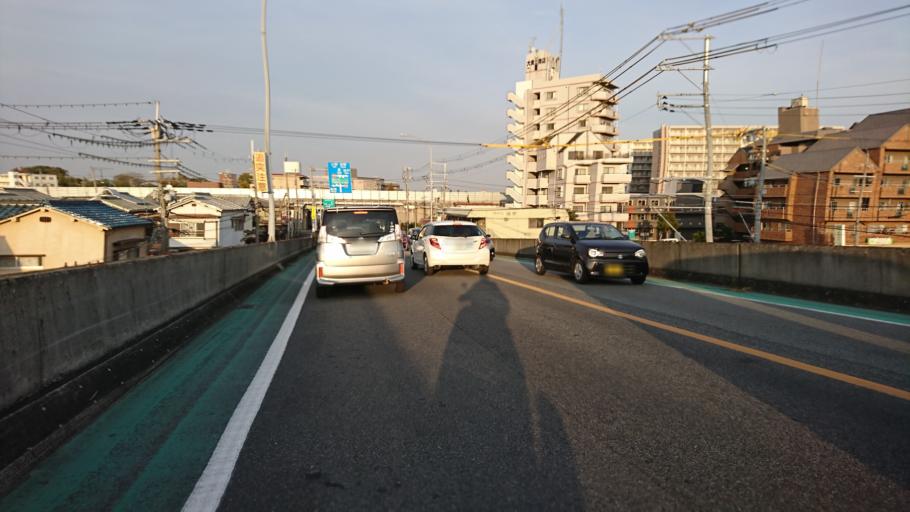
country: JP
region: Hyogo
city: Kakogawacho-honmachi
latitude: 34.7487
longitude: 134.8672
